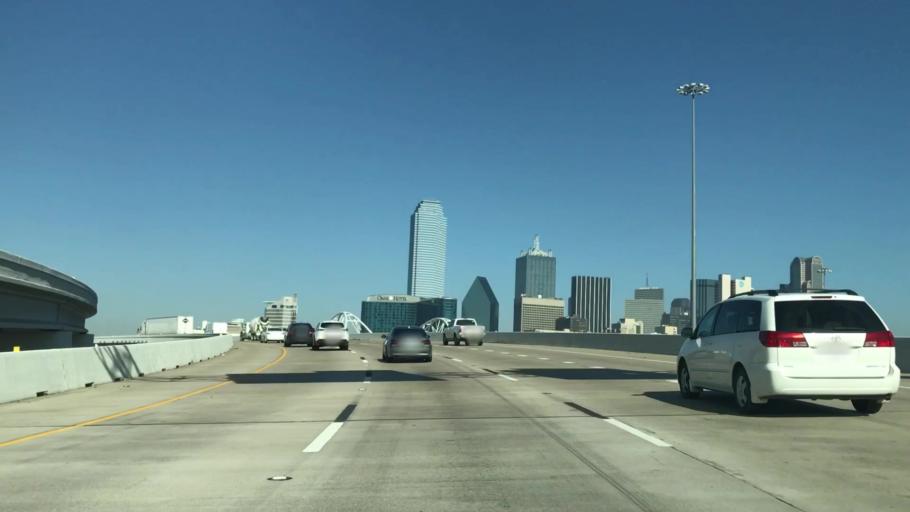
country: US
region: Texas
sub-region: Dallas County
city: Dallas
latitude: 32.7673
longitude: -96.8041
